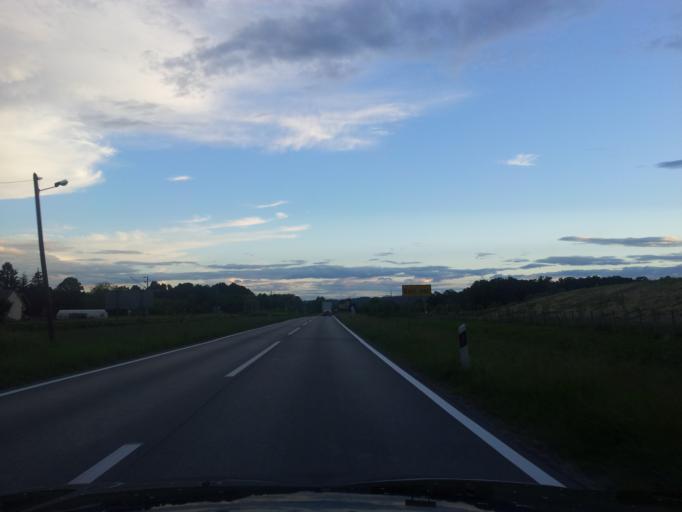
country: HR
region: Karlovacka
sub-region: Grad Karlovac
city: Karlovac
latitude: 45.5275
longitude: 15.5613
